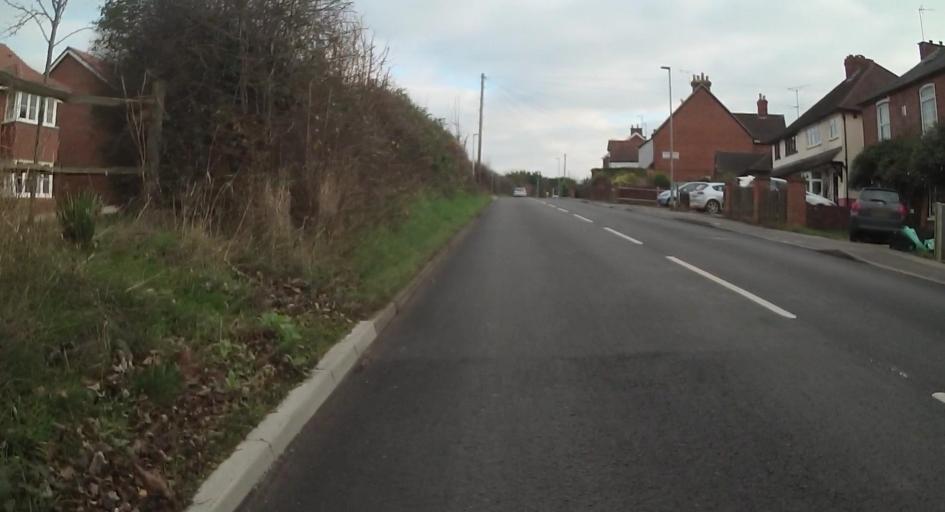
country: GB
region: England
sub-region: Wokingham
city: Wokingham
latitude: 51.4228
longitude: -0.8486
